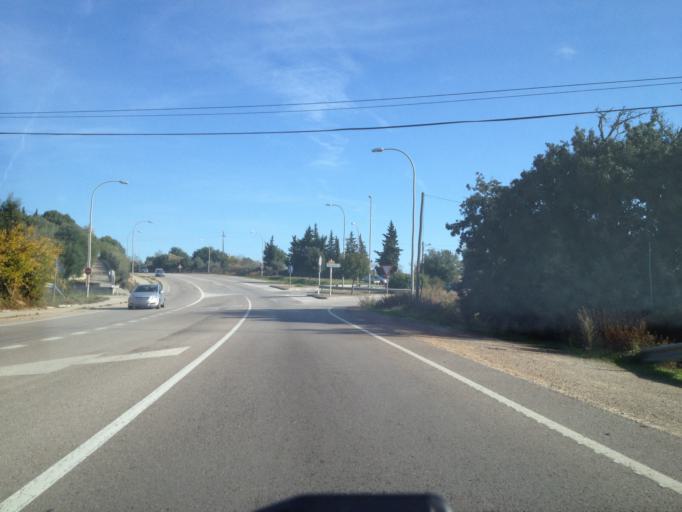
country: ES
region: Balearic Islands
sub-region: Illes Balears
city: Son Servera
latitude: 39.6285
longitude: 3.3583
